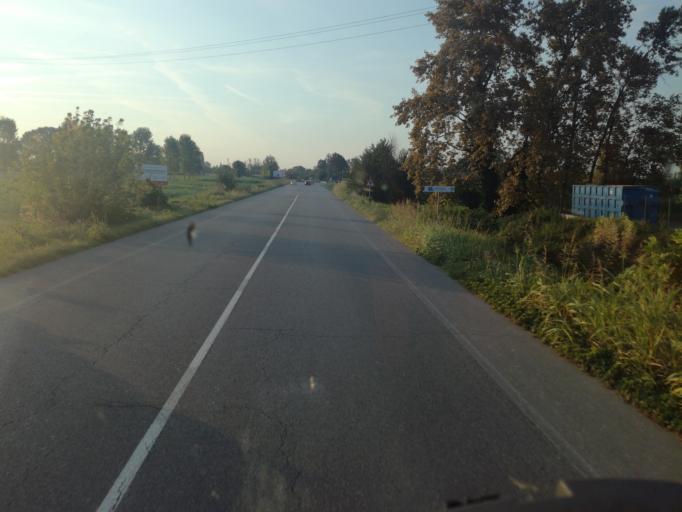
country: IT
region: Lombardy
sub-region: Provincia di Lodi
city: Zelo Buon Persico
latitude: 45.4085
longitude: 9.4439
